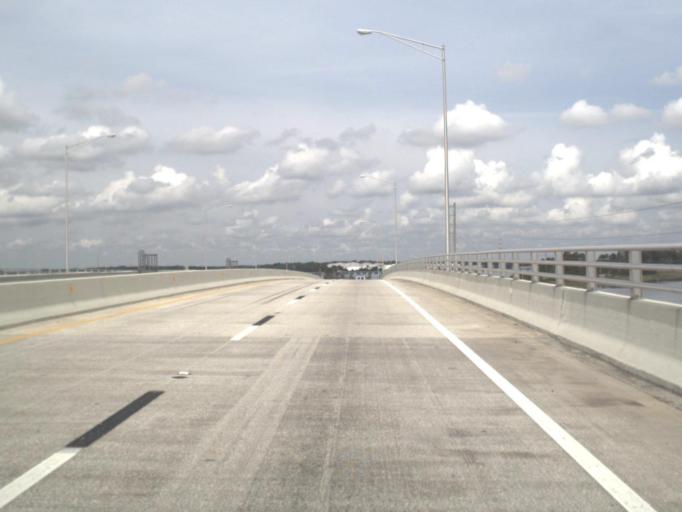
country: US
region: Florida
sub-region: Duval County
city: Jacksonville
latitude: 30.4123
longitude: -81.5818
